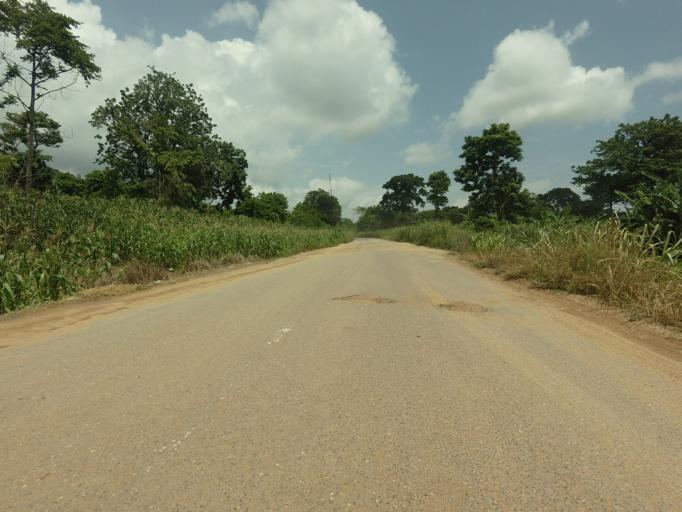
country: GH
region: Volta
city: Ho
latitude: 6.7195
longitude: 0.3402
